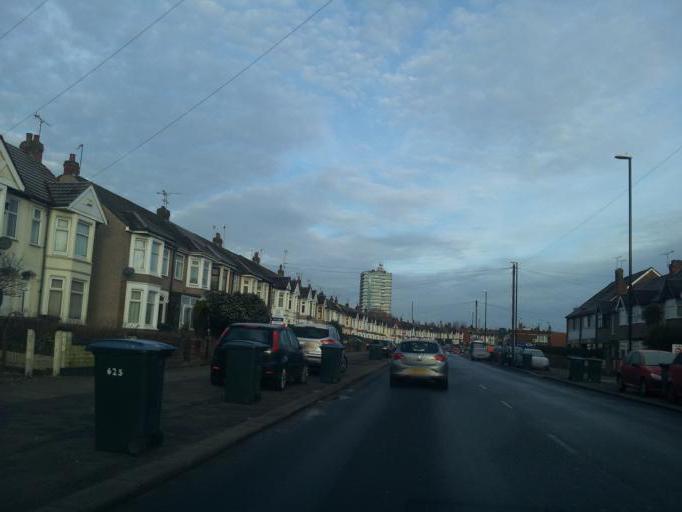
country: GB
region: England
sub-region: Warwickshire
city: Exhall
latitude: 52.4286
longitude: -1.4780
